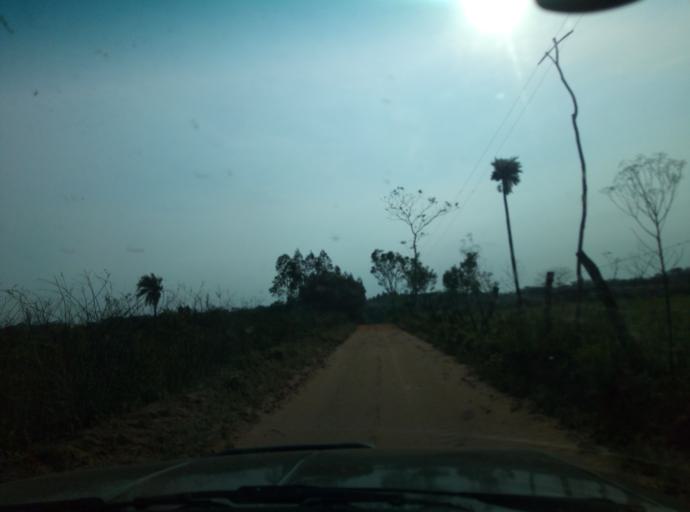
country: PY
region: Caaguazu
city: San Joaquin
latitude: -25.1549
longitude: -56.1059
